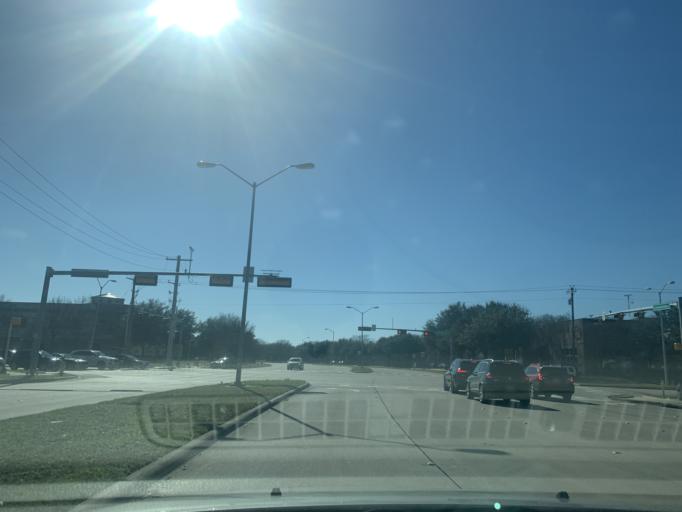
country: US
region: Texas
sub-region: Denton County
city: The Colony
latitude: 33.0561
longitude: -96.8333
